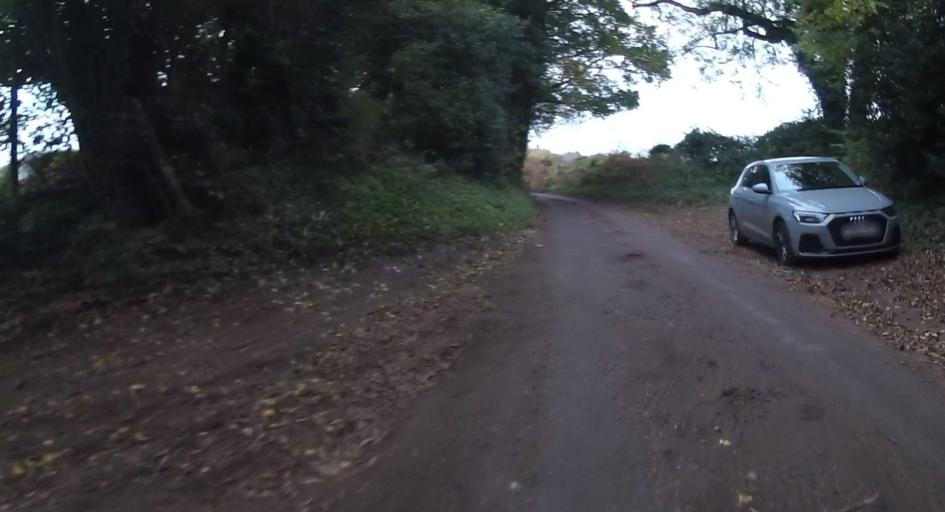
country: GB
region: England
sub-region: Surrey
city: Churt
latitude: 51.1368
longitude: -0.7973
